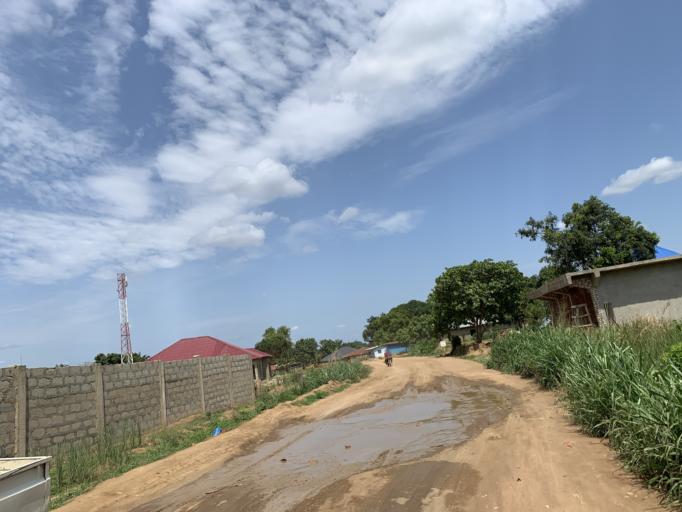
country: SL
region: Western Area
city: Waterloo
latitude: 8.3257
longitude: -13.0381
